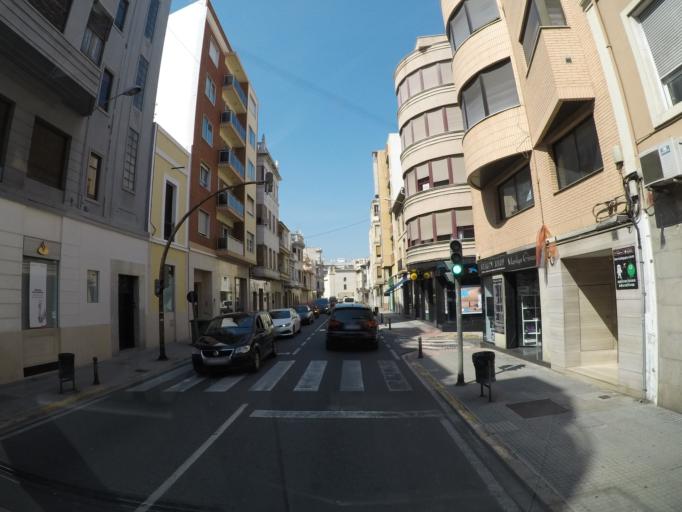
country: ES
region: Valencia
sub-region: Provincia de Valencia
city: Oliva
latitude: 38.9207
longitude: -0.1181
